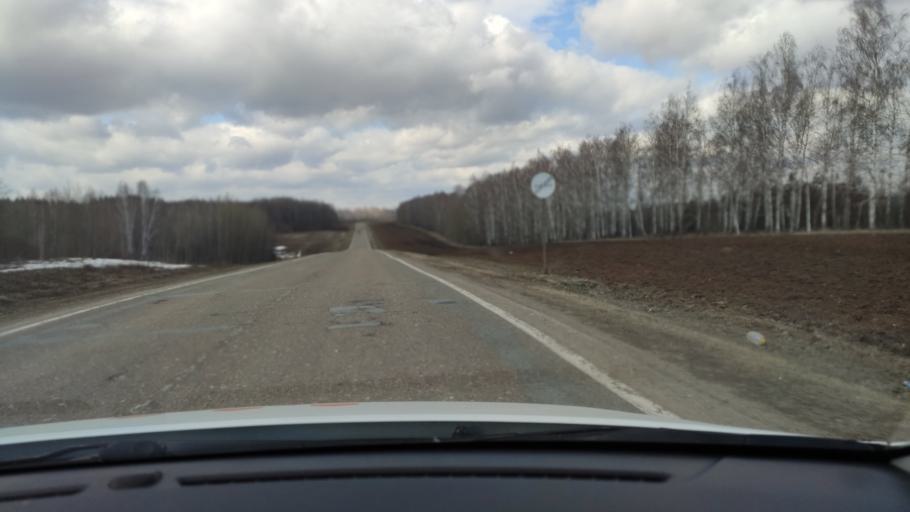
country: RU
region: Tatarstan
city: Vysokaya Gora
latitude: 56.0887
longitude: 49.1813
